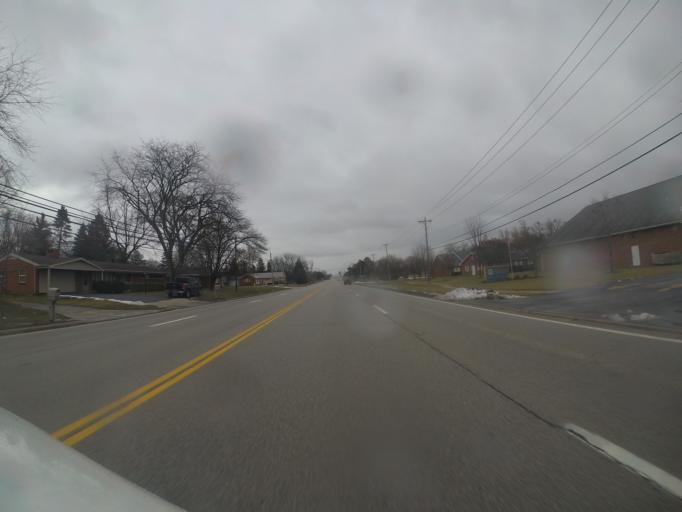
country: US
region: Ohio
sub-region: Wood County
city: Perrysburg
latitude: 41.5650
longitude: -83.5960
